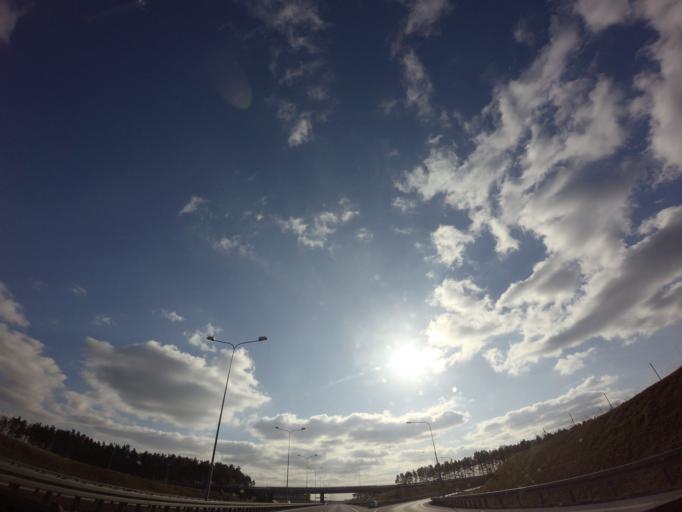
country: PL
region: Lubusz
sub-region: Powiat swiebodzinski
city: Swiebodzin
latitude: 52.3203
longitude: 15.5502
